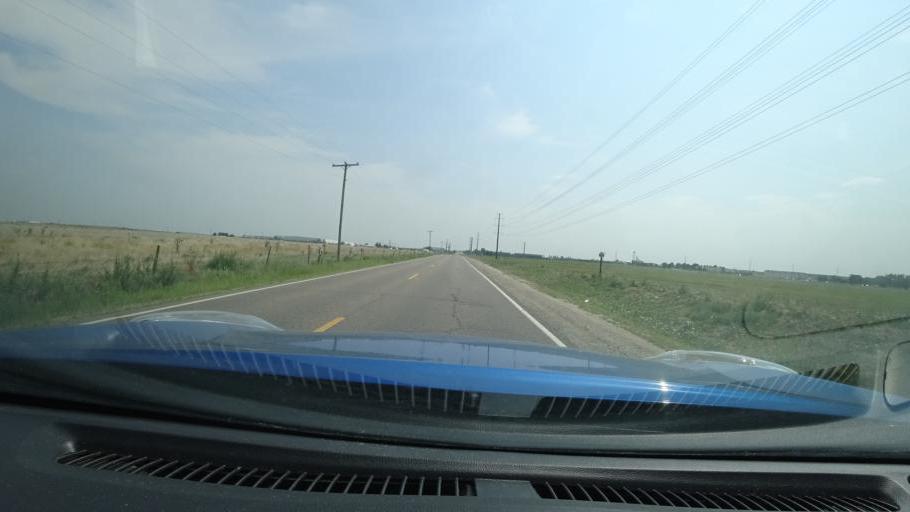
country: US
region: Colorado
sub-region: Adams County
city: Aurora
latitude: 39.7618
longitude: -104.7347
